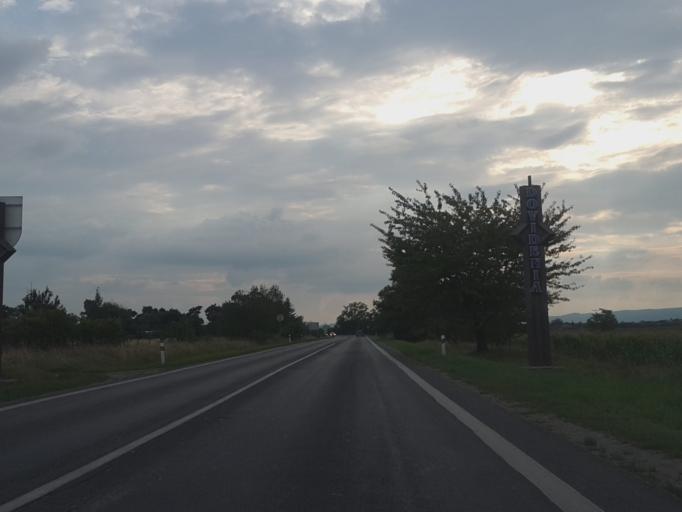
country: SK
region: Bratislavsky
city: Senec
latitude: 48.2124
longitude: 17.3780
